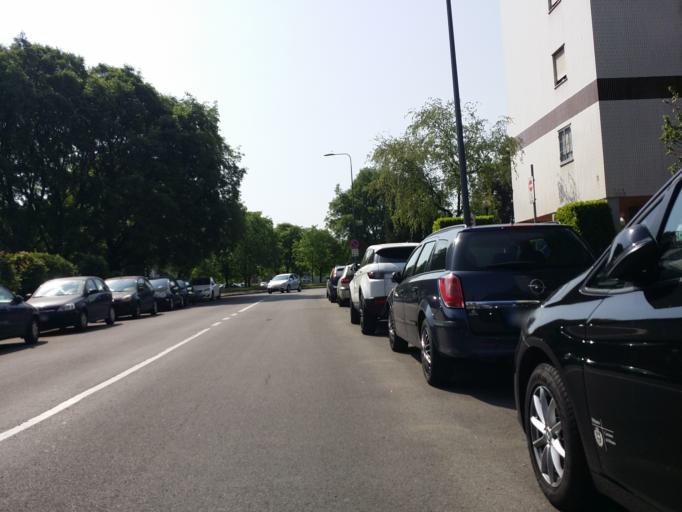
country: IT
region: Lombardy
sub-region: Citta metropolitana di Milano
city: Romano Banco
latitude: 45.4568
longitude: 9.1137
